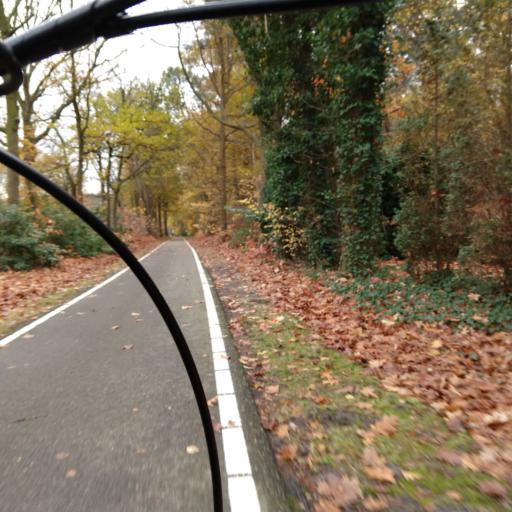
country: BE
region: Flanders
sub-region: Provincie Antwerpen
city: Stabroek
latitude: 51.3755
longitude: 4.3820
